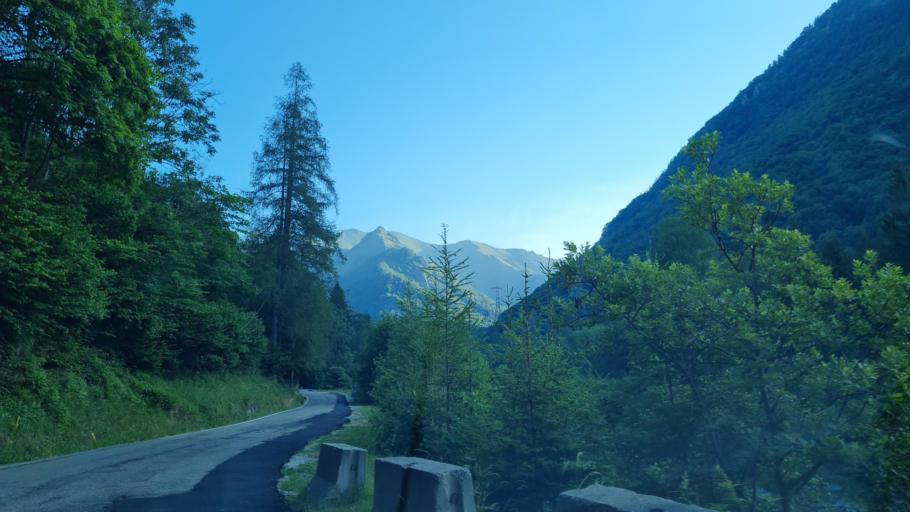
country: IT
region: Piedmont
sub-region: Provincia di Torino
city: Ronco Canavese
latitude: 45.5107
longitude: 7.5505
